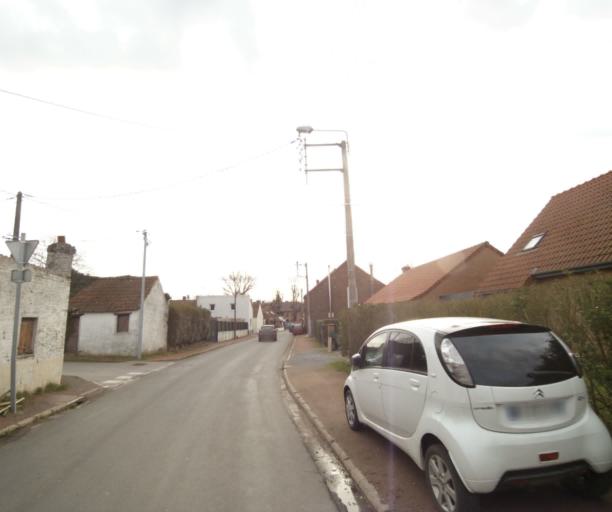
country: FR
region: Nord-Pas-de-Calais
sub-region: Departement du Nord
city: Hergnies
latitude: 50.4770
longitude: 3.5220
